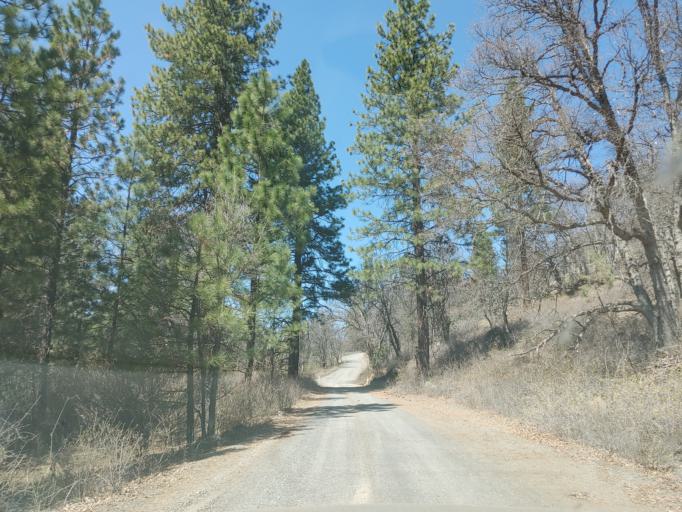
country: US
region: California
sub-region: Shasta County
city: Burney
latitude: 41.0176
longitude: -121.6205
